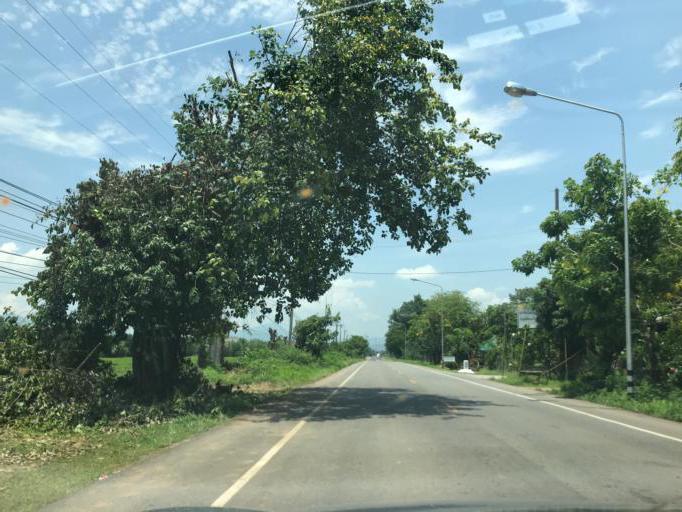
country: TH
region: Phayao
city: Phu Sang
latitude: 19.5832
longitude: 100.3067
